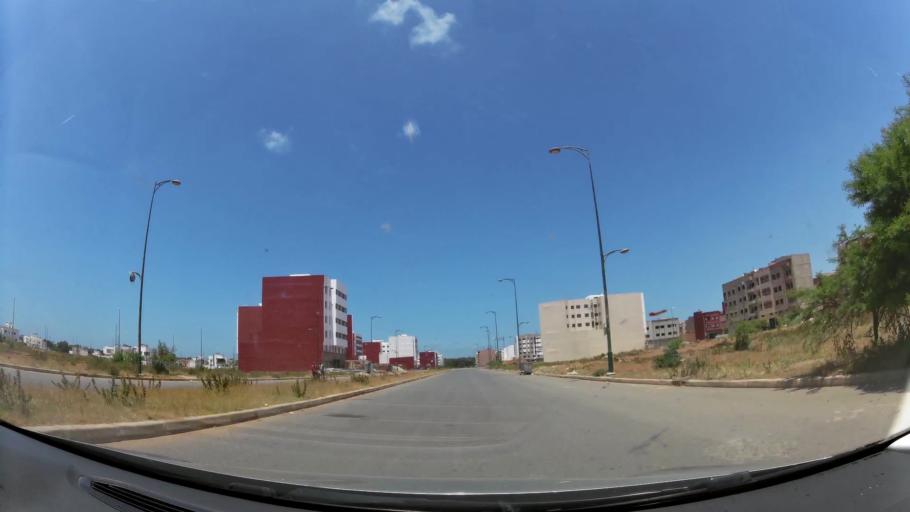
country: MA
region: Gharb-Chrarda-Beni Hssen
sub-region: Kenitra Province
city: Kenitra
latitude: 34.2658
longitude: -6.6262
